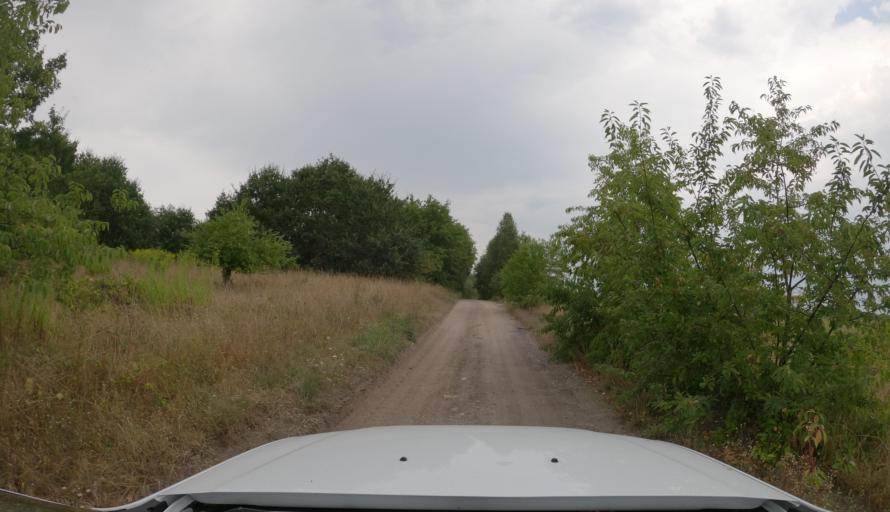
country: PL
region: West Pomeranian Voivodeship
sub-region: Powiat drawski
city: Drawsko Pomorskie
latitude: 53.5136
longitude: 15.7912
